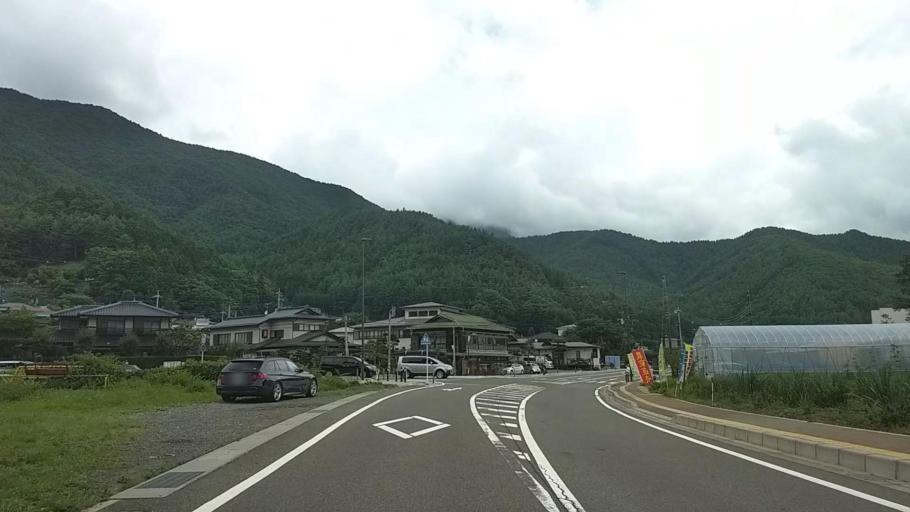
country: JP
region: Yamanashi
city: Fujikawaguchiko
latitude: 35.5075
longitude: 138.7156
